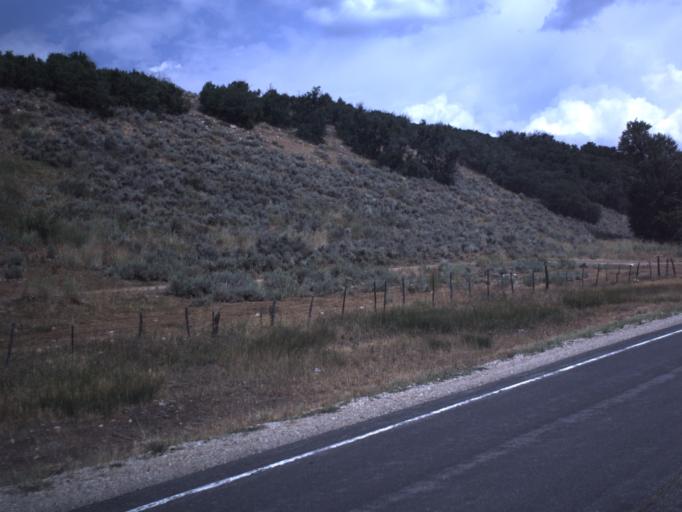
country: US
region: Utah
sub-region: Summit County
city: Francis
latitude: 40.5569
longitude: -111.1442
